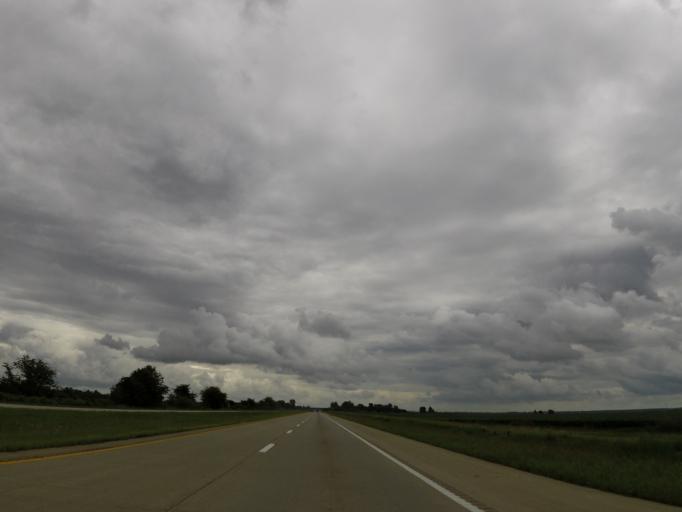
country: US
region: Missouri
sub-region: Mississippi County
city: Charleston
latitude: 36.9584
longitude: -89.2753
